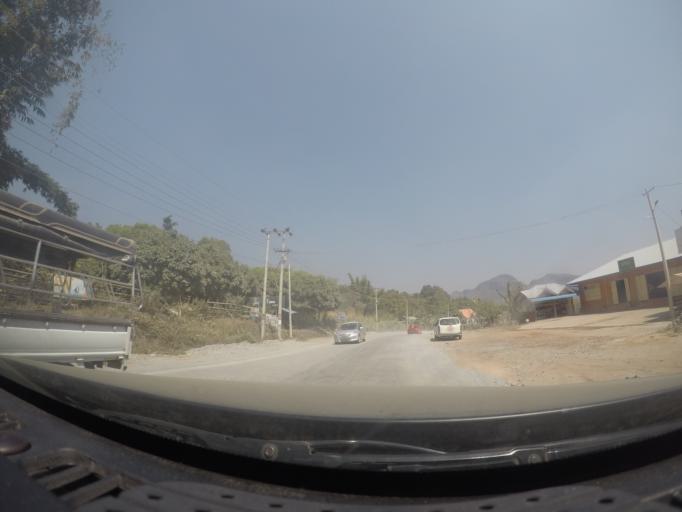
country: MM
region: Shan
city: Taunggyi
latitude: 20.7719
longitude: 97.1224
